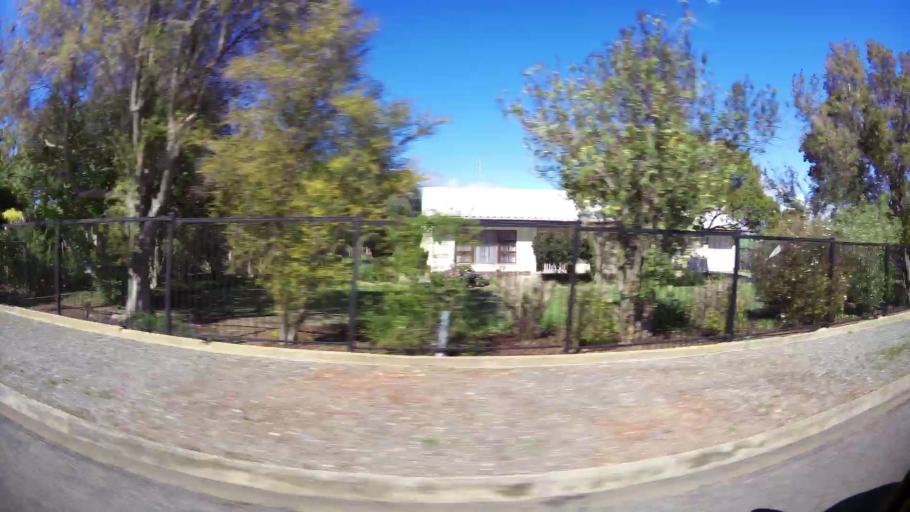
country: ZA
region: Western Cape
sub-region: Cape Winelands District Municipality
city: Ashton
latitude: -33.8065
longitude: 19.8958
